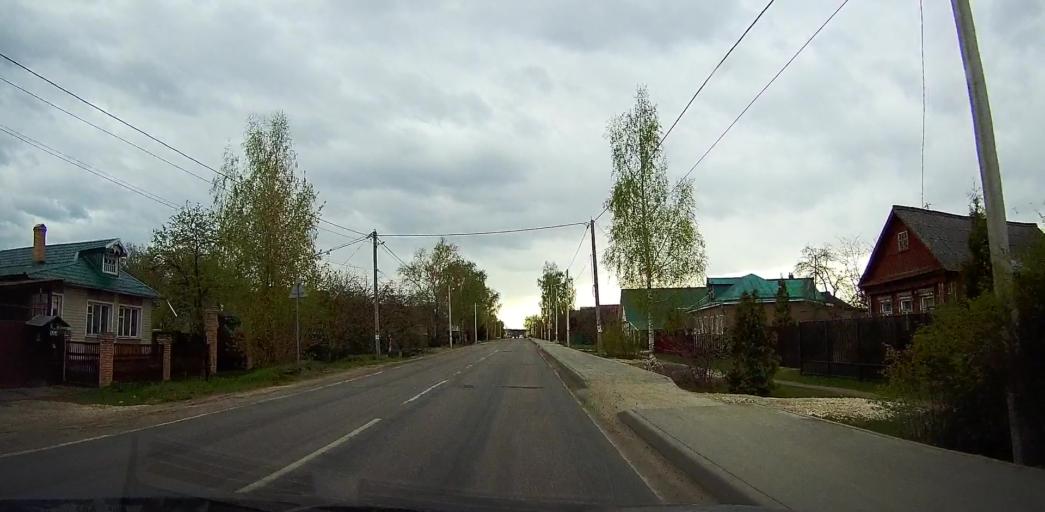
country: RU
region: Moskovskaya
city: Pavlovskiy Posad
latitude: 55.7573
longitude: 38.7080
